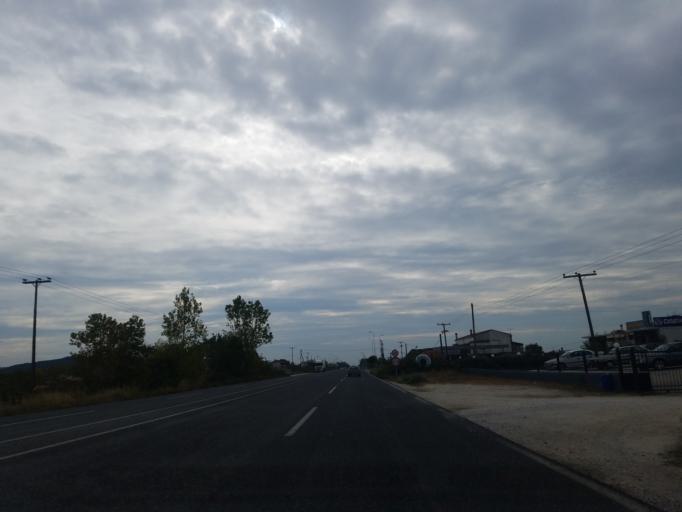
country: GR
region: Thessaly
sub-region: Trikala
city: Kalampaka
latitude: 39.6767
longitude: 21.6591
